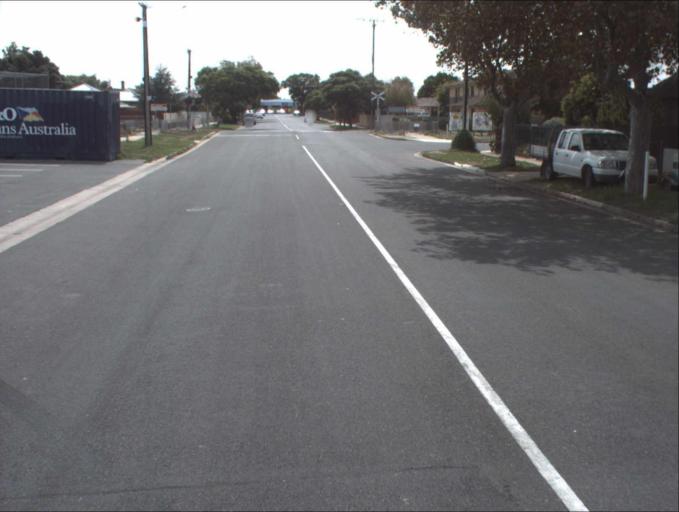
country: AU
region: South Australia
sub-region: Port Adelaide Enfield
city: Alberton
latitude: -34.8542
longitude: 138.5216
